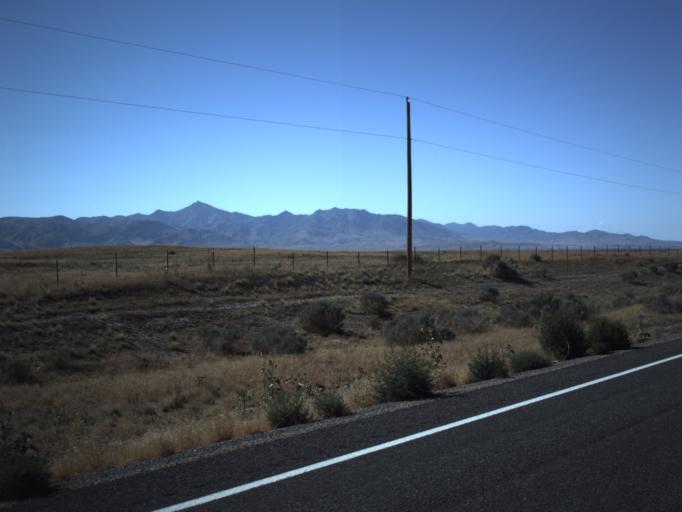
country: US
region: Utah
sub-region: Millard County
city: Delta
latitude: 39.5971
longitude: -112.3268
